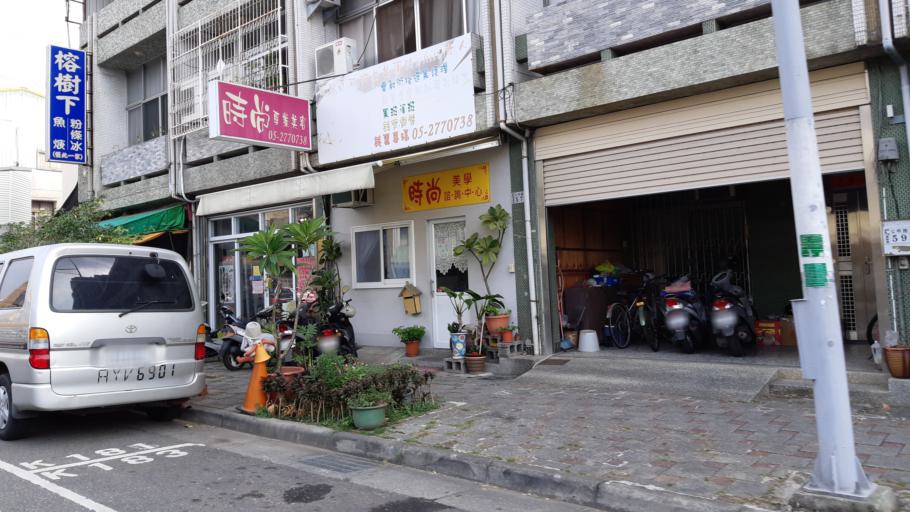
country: TW
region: Taiwan
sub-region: Chiayi
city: Jiayi Shi
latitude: 23.4806
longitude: 120.4593
